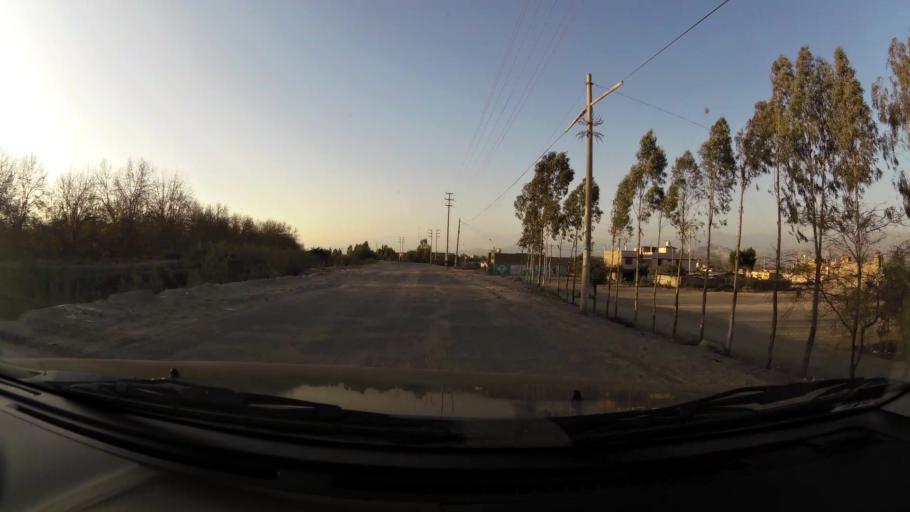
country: PE
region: Ica
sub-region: Provincia de Ica
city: Ica
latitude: -14.0862
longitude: -75.7176
